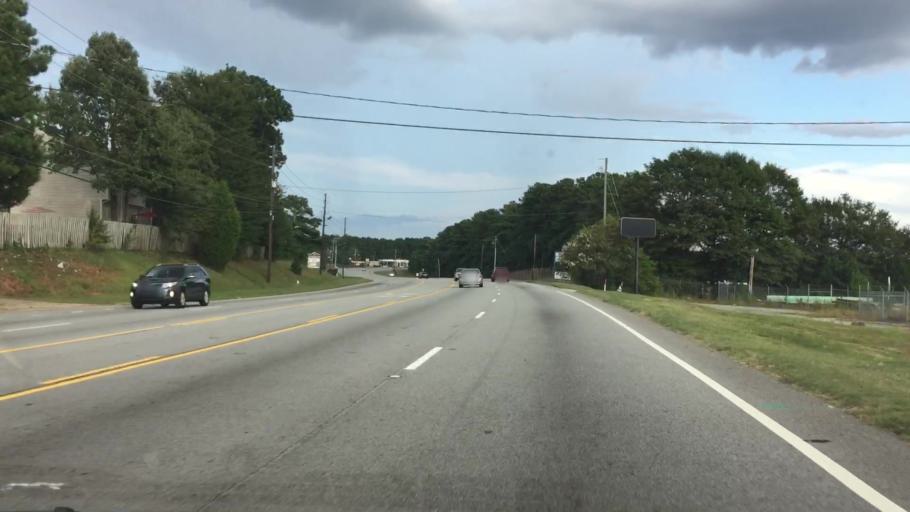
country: US
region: Georgia
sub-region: Clayton County
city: Riverdale
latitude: 33.5477
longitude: -84.4110
